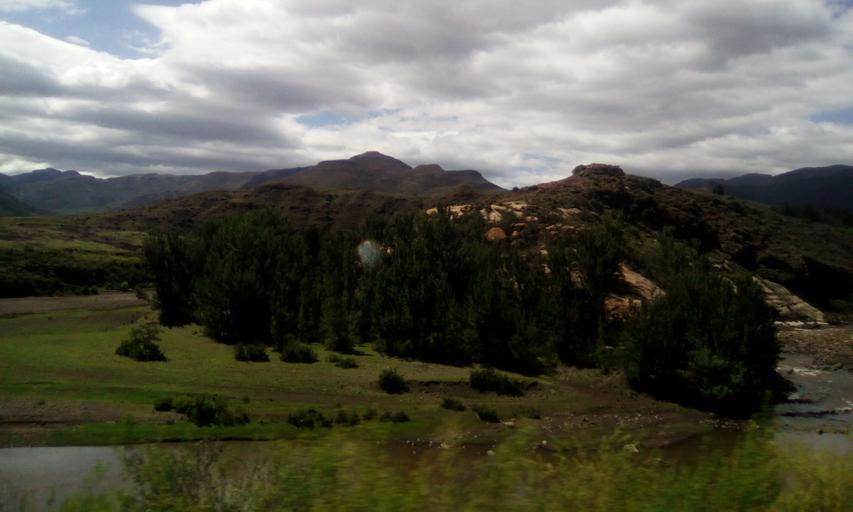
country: LS
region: Maseru
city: Nako
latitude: -29.6637
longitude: 27.8009
